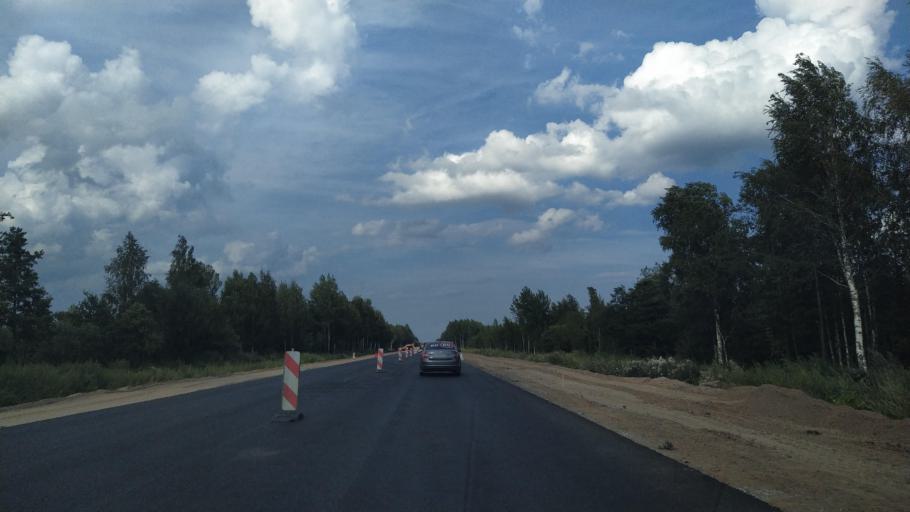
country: RU
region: Novgorod
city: Shimsk
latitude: 58.2927
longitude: 30.8626
